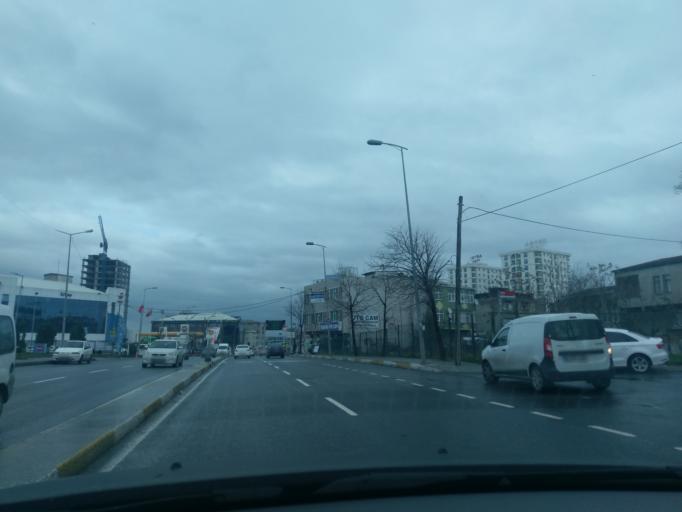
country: TR
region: Istanbul
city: Mahmutbey
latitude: 41.0584
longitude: 28.8312
